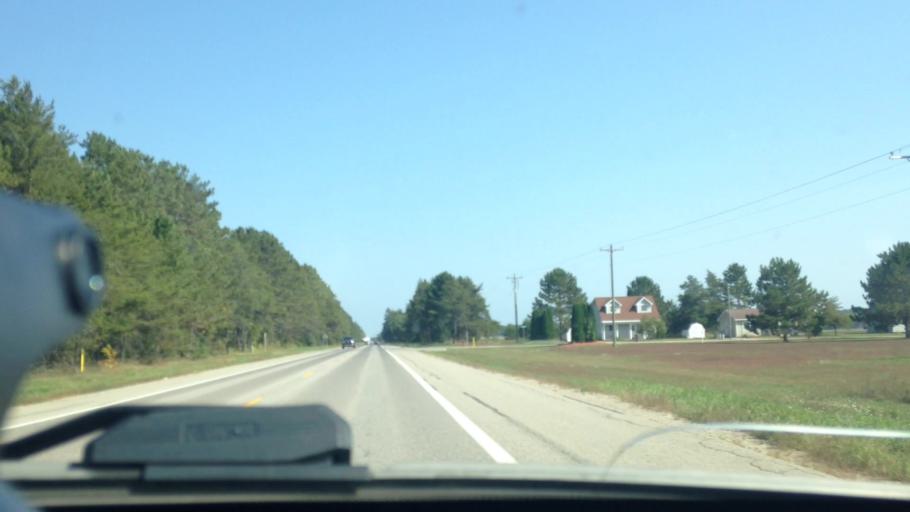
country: US
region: Michigan
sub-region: Luce County
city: Newberry
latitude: 46.3034
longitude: -85.4858
